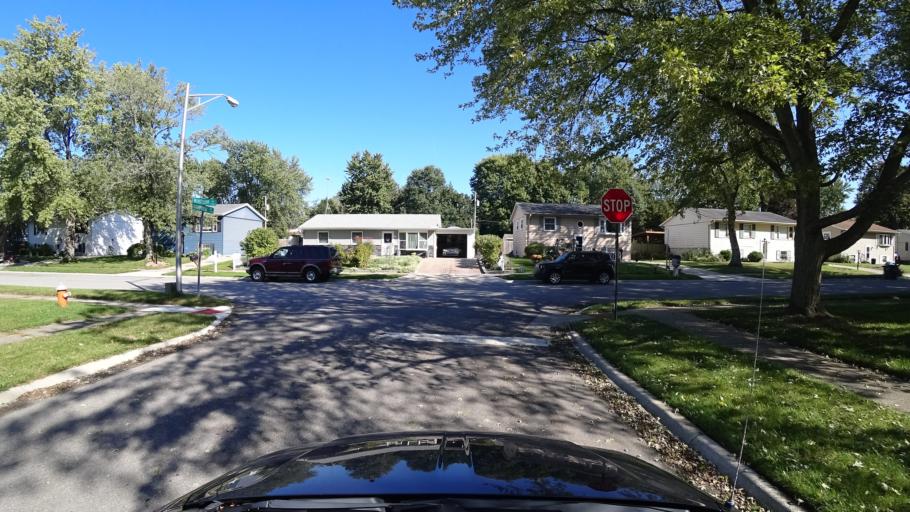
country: US
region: Indiana
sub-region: LaPorte County
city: Michigan City
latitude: 41.6911
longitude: -86.9048
